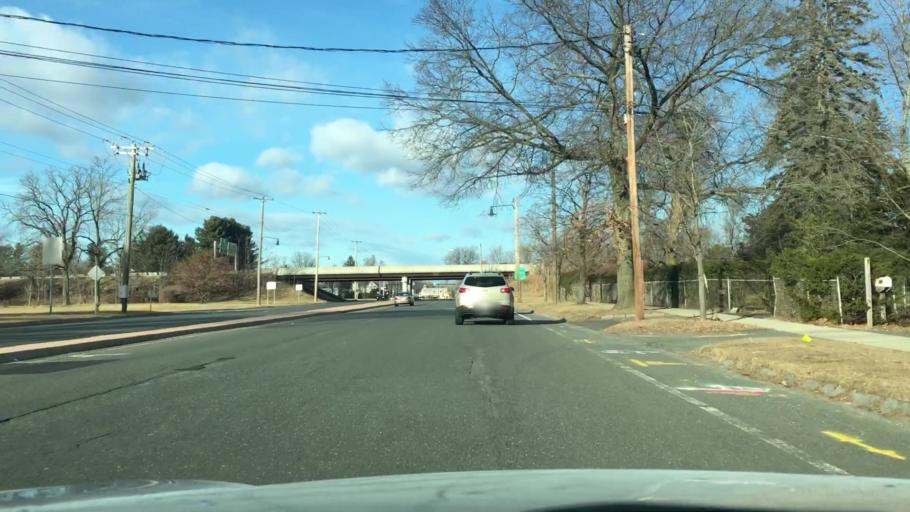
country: US
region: Massachusetts
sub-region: Hampden County
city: Agawam
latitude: 42.0740
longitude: -72.6145
